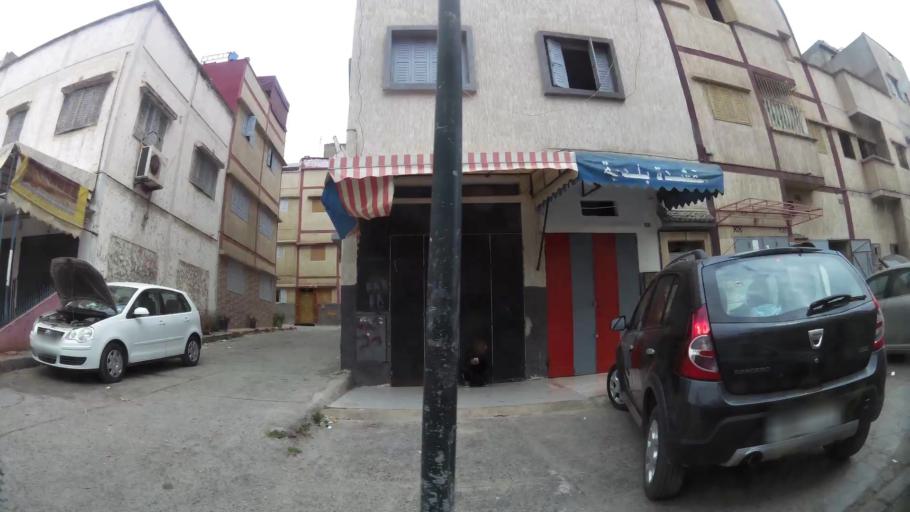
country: MA
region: Rabat-Sale-Zemmour-Zaer
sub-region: Rabat
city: Rabat
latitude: 33.9931
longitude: -6.8727
